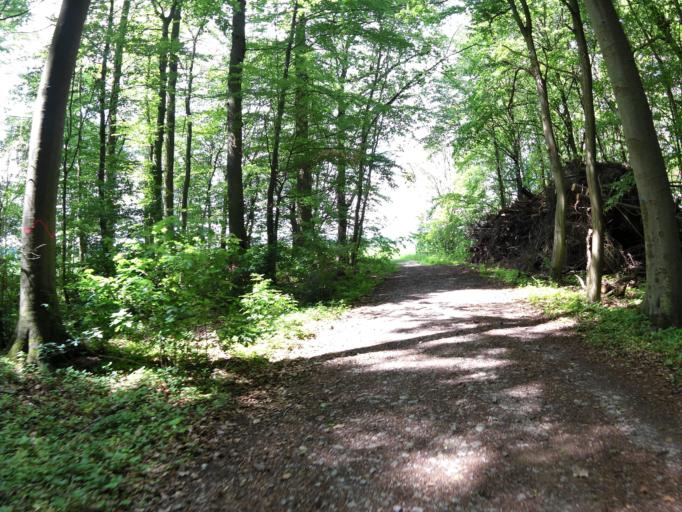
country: DE
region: Bavaria
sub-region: Regierungsbezirk Unterfranken
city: Kist
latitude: 49.7367
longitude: 9.8533
